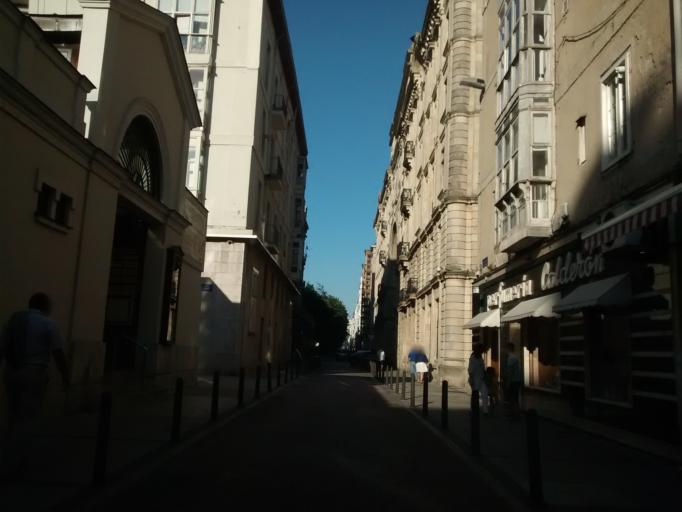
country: ES
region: Cantabria
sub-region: Provincia de Cantabria
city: Santander
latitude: 43.4622
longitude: -3.8043
